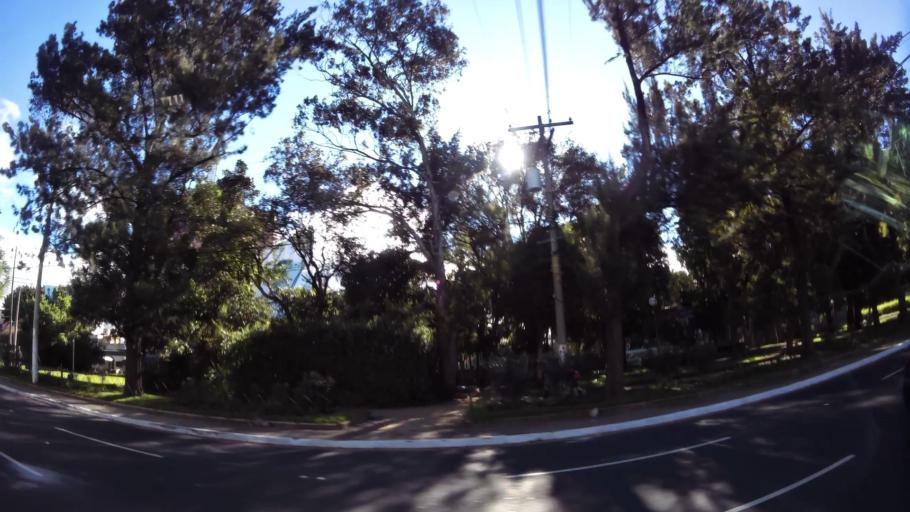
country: GT
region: Guatemala
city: Santa Catarina Pinula
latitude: 14.5932
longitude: -90.5184
